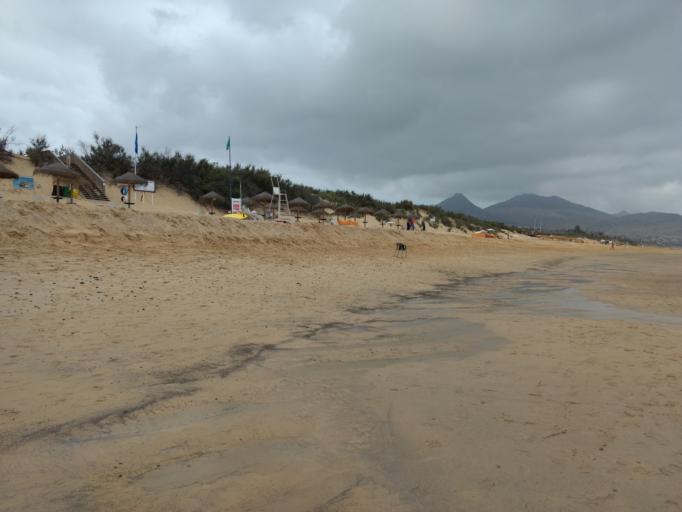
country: PT
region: Madeira
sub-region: Porto Santo
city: Vila de Porto Santo
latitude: 33.0406
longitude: -16.3551
